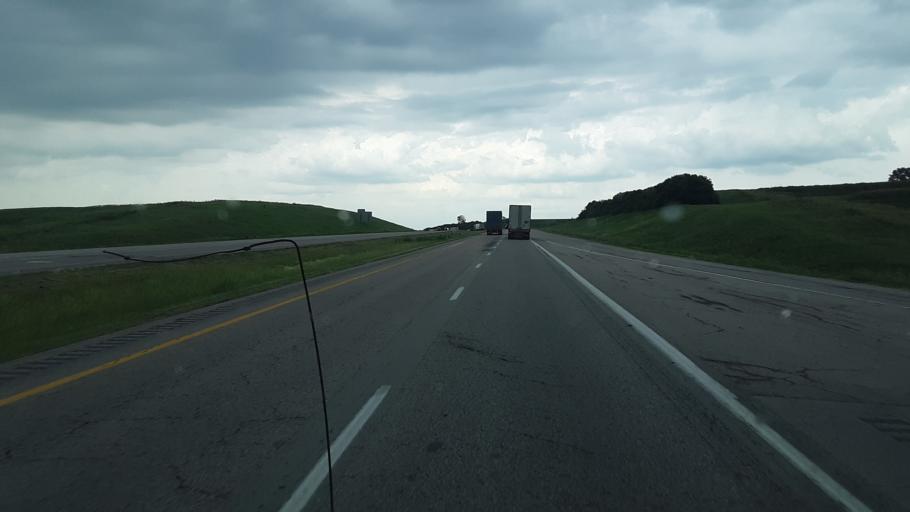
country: US
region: Iowa
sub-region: Pottawattamie County
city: Council Bluffs
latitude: 41.3786
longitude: -95.6730
